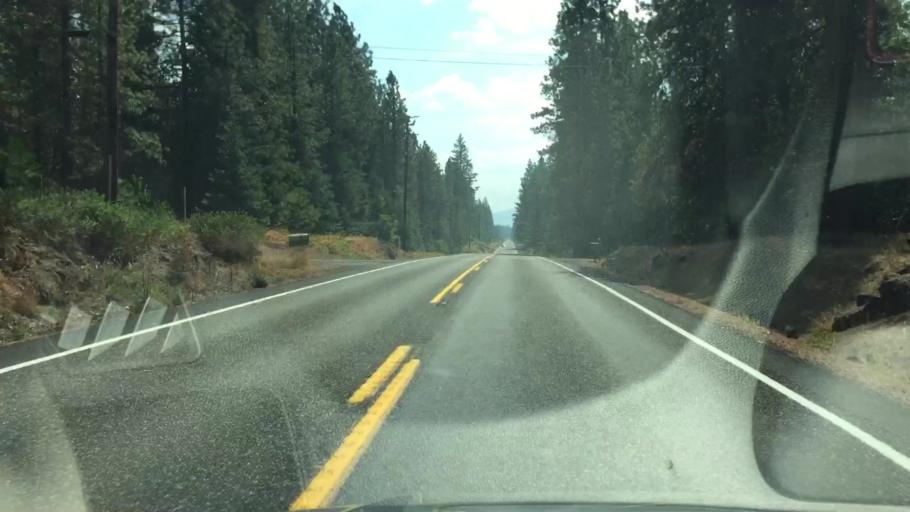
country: US
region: Washington
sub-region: Klickitat County
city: White Salmon
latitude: 45.9387
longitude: -121.4926
